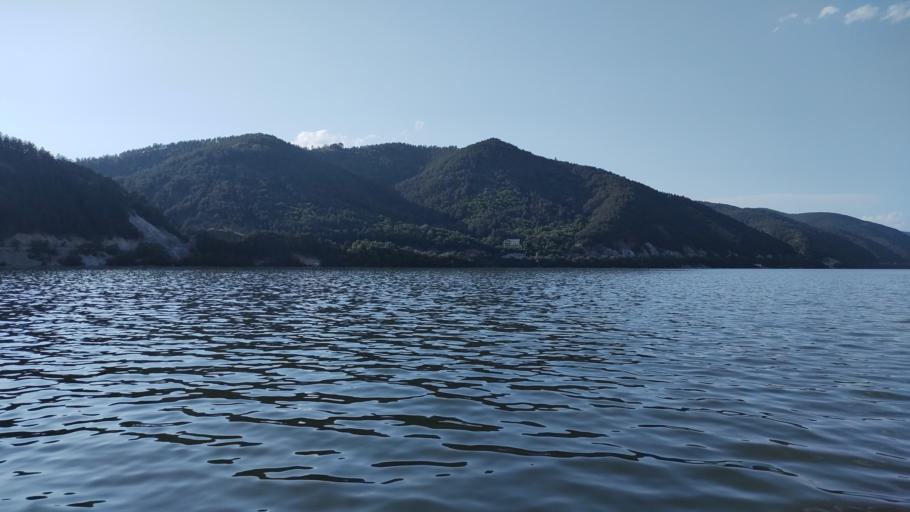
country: RO
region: Mehedinti
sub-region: Comuna Svinita
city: Svinita
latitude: 44.5129
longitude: 22.1996
